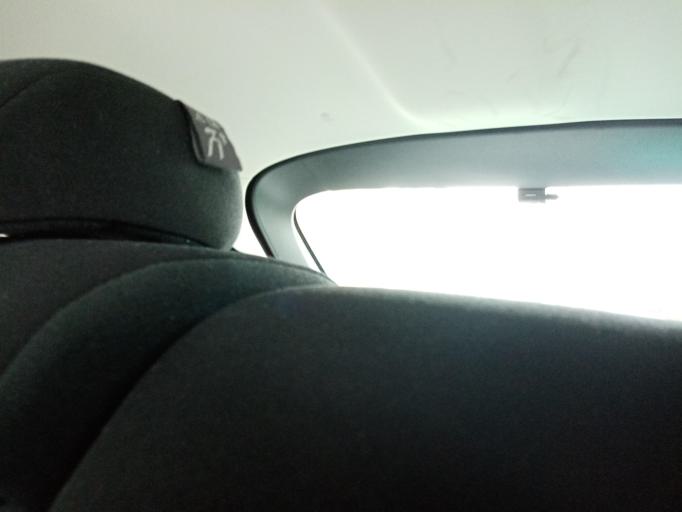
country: AU
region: Western Australia
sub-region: City of Cockburn
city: Success
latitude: -32.1305
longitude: 115.8528
